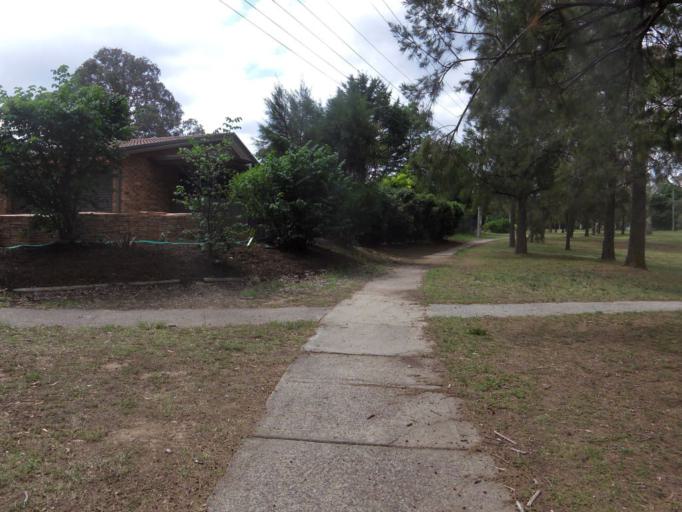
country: AU
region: Australian Capital Territory
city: Macarthur
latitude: -35.4082
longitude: 149.1279
